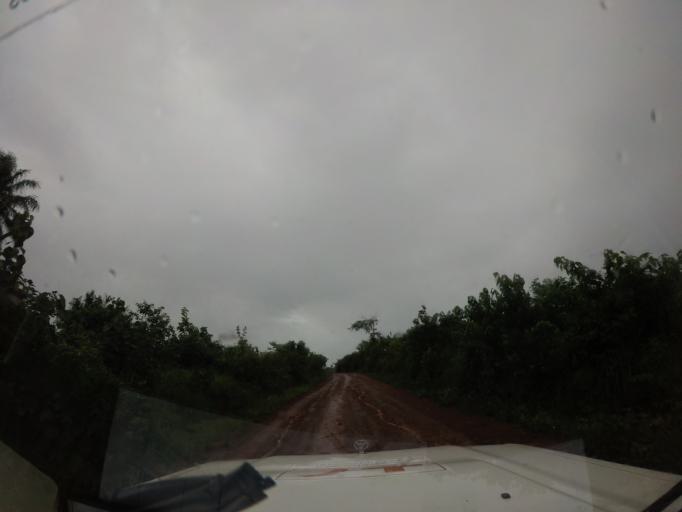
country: SL
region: Eastern Province
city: Kenema
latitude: 7.7349
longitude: -11.1908
